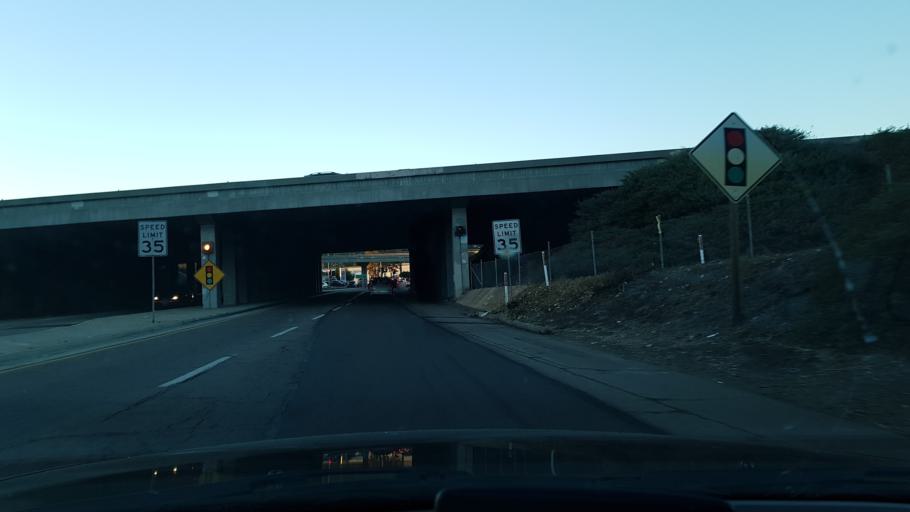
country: US
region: California
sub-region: San Diego County
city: Lemon Grove
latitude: 32.7785
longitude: -117.1008
